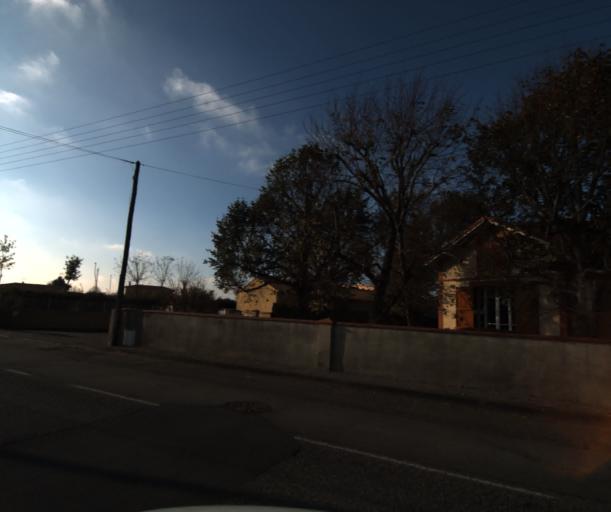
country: FR
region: Midi-Pyrenees
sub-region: Departement de la Haute-Garonne
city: Colomiers
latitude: 43.5970
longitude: 1.3588
